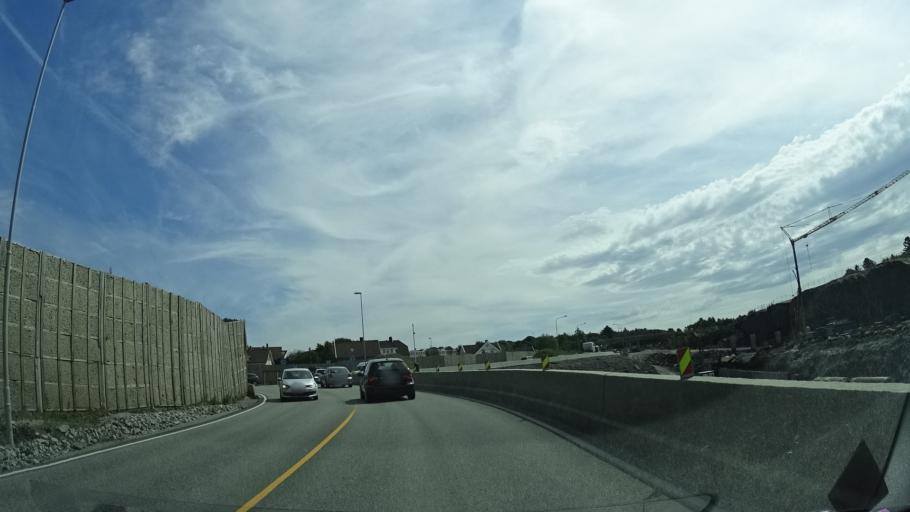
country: NO
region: Rogaland
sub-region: Stavanger
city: Stavanger
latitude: 58.9790
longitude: 5.6864
